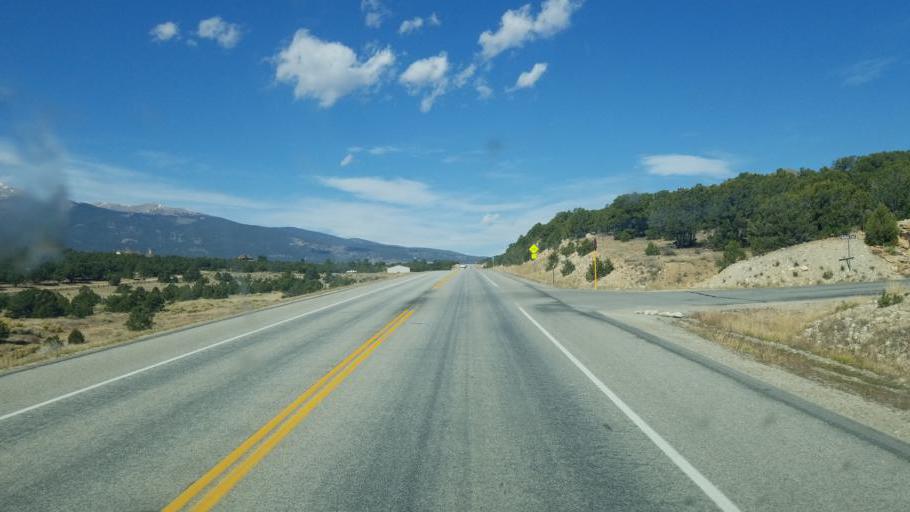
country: US
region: Colorado
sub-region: Chaffee County
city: Buena Vista
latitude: 38.8652
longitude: -106.1517
